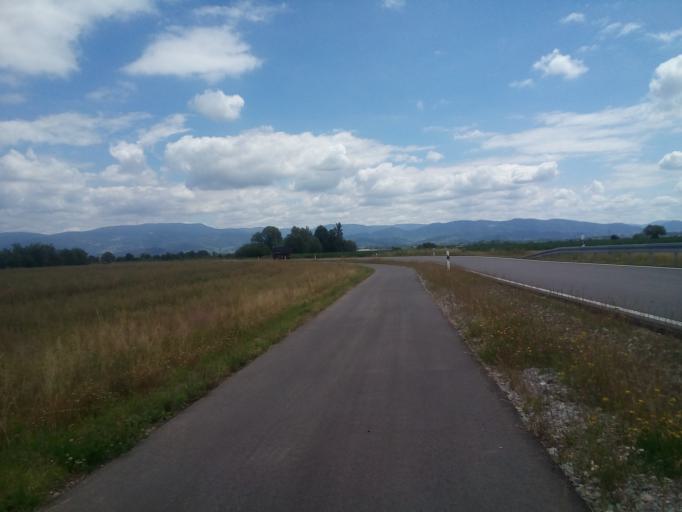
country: DE
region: Baden-Wuerttemberg
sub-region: Freiburg Region
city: Renchen
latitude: 48.6155
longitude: 7.9783
